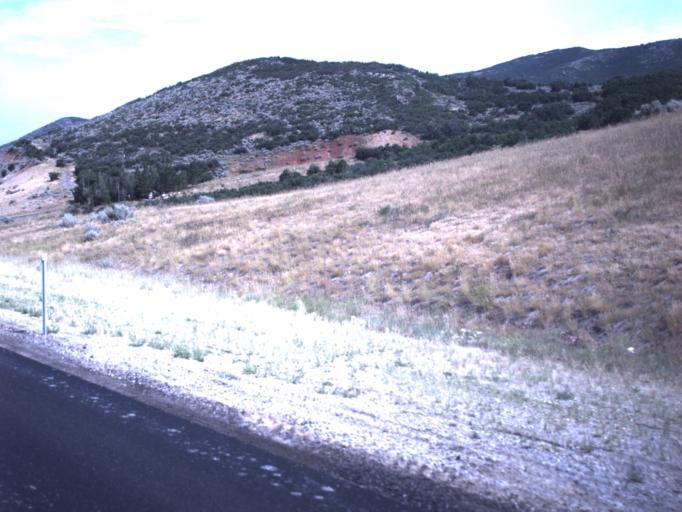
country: US
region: Utah
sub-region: Summit County
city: Park City
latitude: 40.6362
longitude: -111.3946
